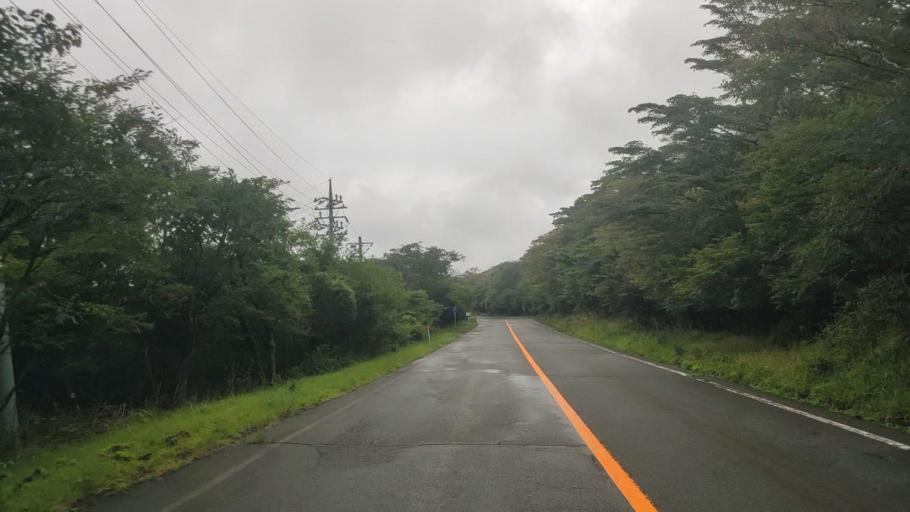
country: JP
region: Shizuoka
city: Fuji
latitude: 35.2916
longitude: 138.7768
